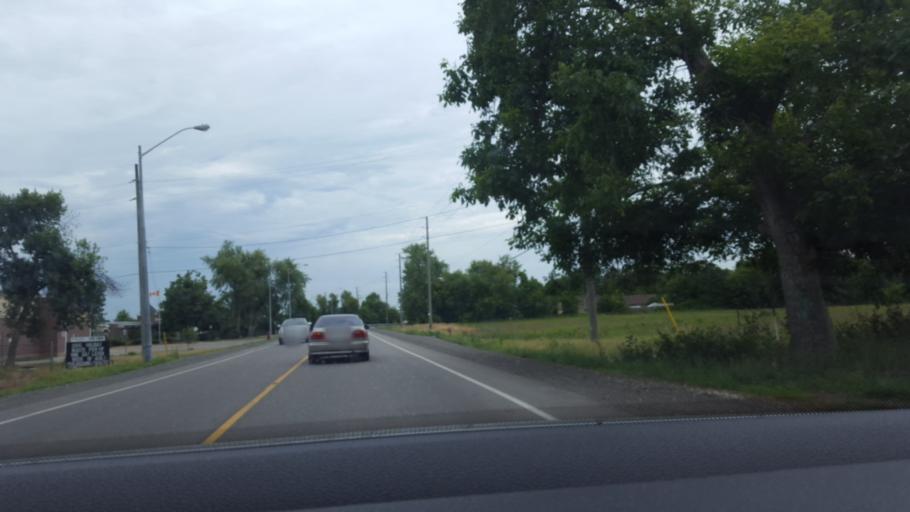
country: CA
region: Ontario
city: Brampton
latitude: 43.6401
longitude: -79.8101
